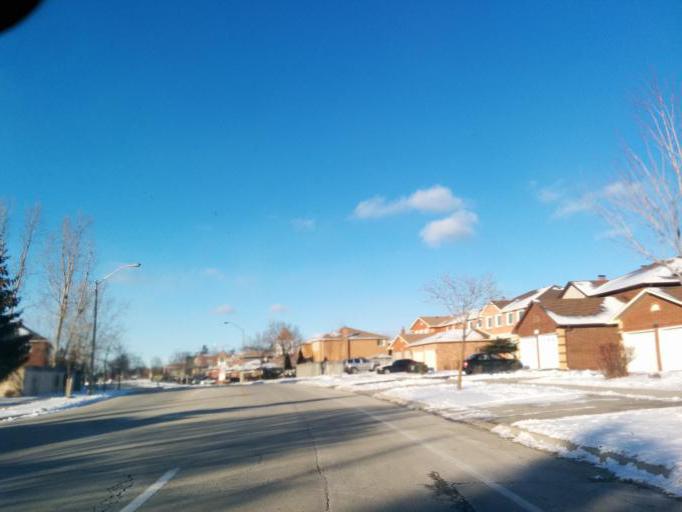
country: CA
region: Ontario
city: Oakville
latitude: 43.4984
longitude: -79.6616
